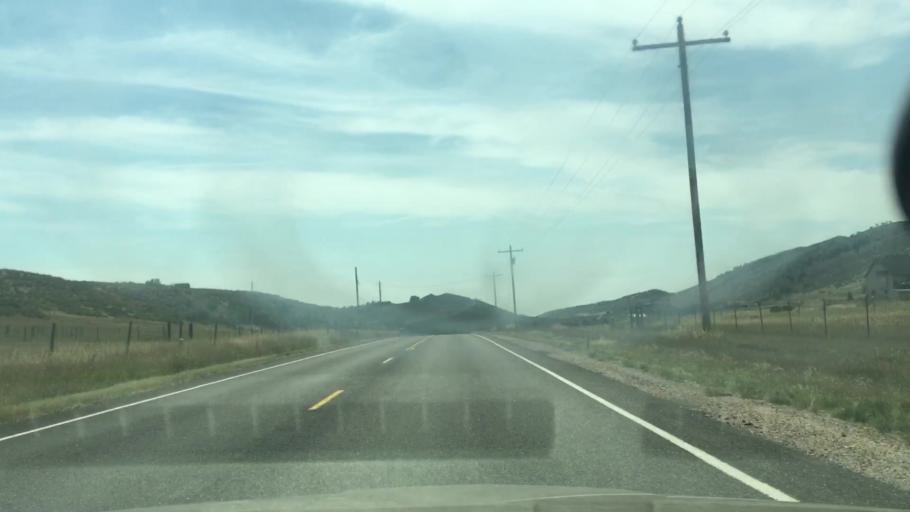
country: US
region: Colorado
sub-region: Larimer County
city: Campion
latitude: 40.3488
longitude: -105.1842
